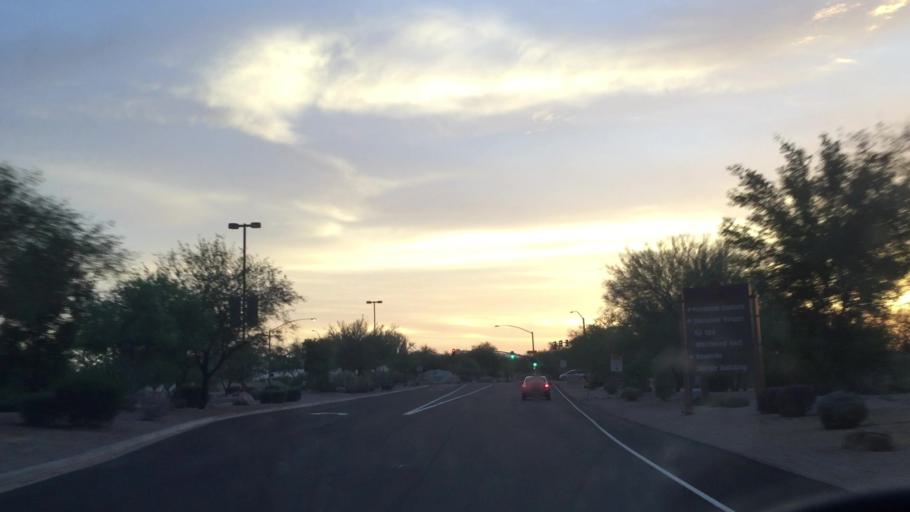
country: US
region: Arizona
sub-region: Maricopa County
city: Guadalupe
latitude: 33.2768
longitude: -111.9770
